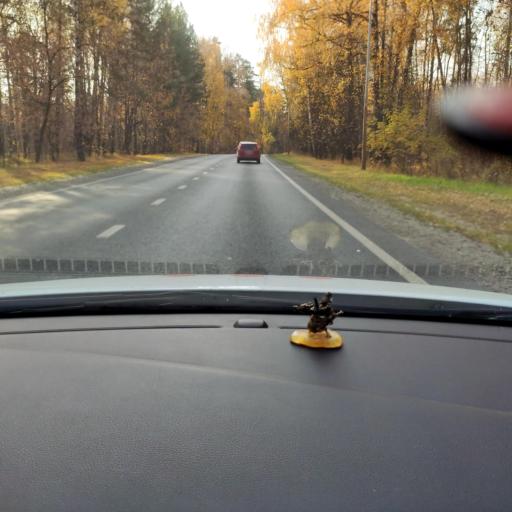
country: RU
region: Tatarstan
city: Osinovo
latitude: 55.8342
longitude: 48.8929
